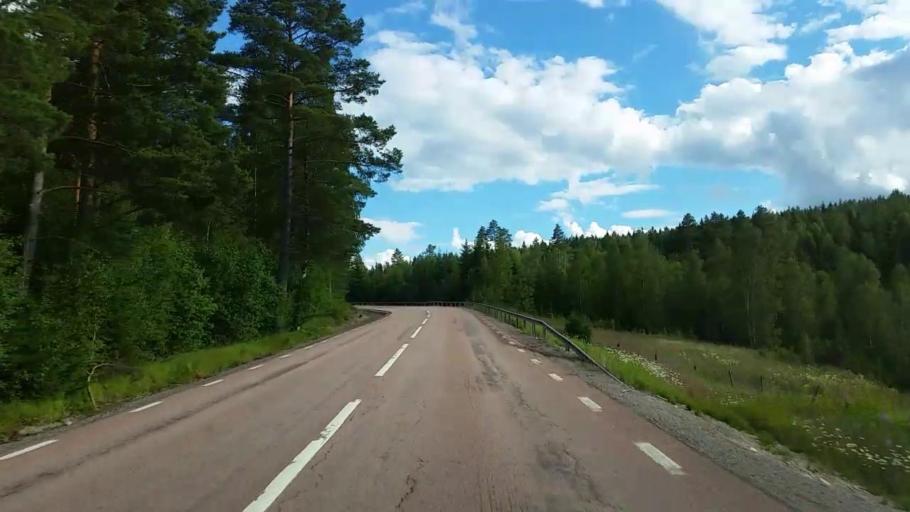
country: SE
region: Gaevleborg
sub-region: Ljusdals Kommun
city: Farila
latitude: 61.8930
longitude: 15.9082
